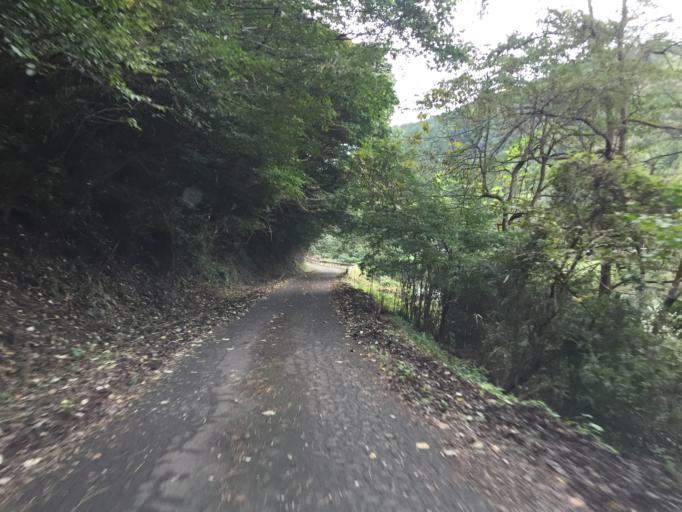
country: JP
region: Miyagi
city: Marumori
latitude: 37.9304
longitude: 140.7263
